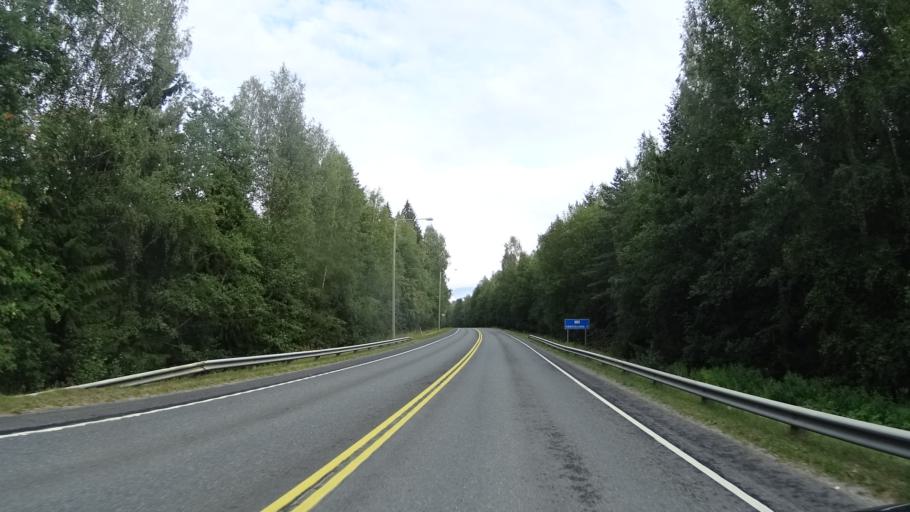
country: FI
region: Haeme
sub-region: Haemeenlinna
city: Parola
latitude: 61.0279
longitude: 24.2840
